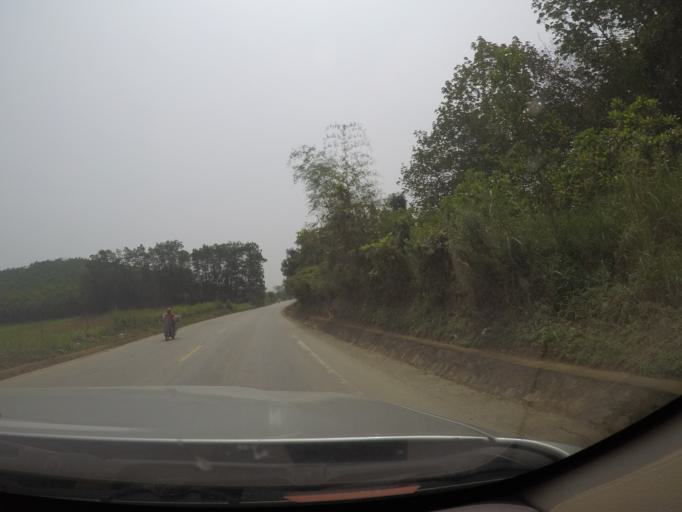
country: VN
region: Thanh Hoa
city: Thi Tran Thuong Xuan
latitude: 19.8777
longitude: 105.4081
